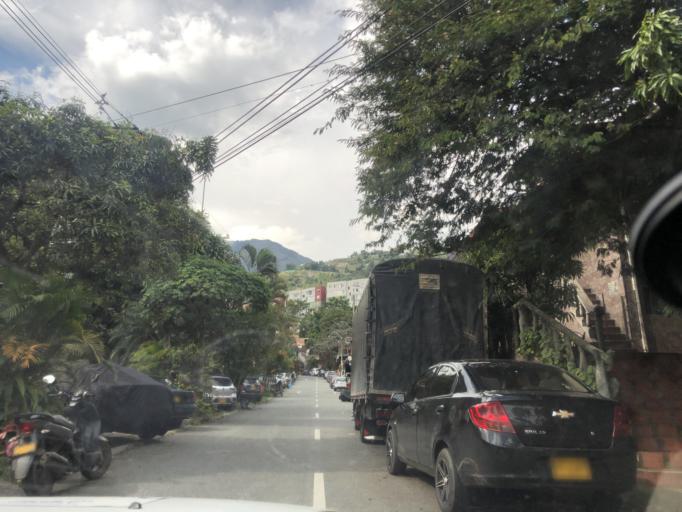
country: CO
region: Antioquia
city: Municipio de Copacabana
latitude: 6.3469
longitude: -75.5319
